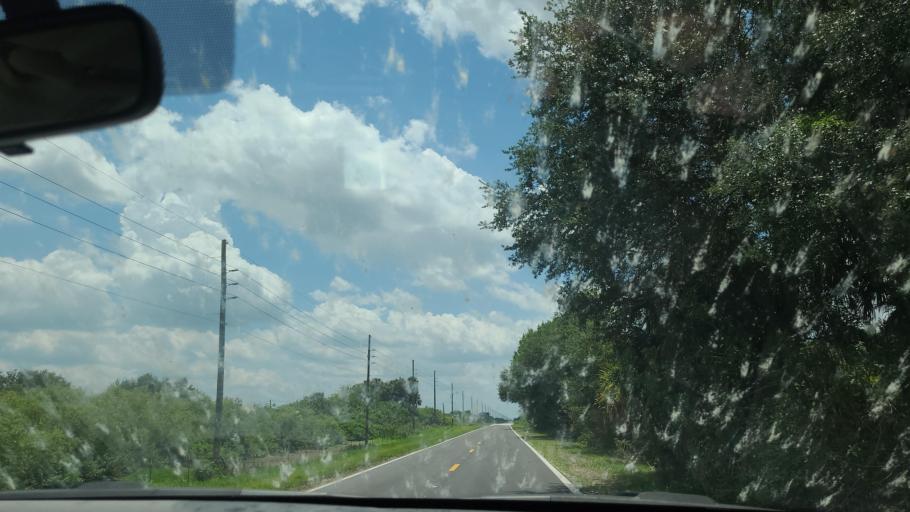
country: US
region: Florida
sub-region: Glades County
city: Buckhead Ridge
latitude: 27.2123
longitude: -81.0945
